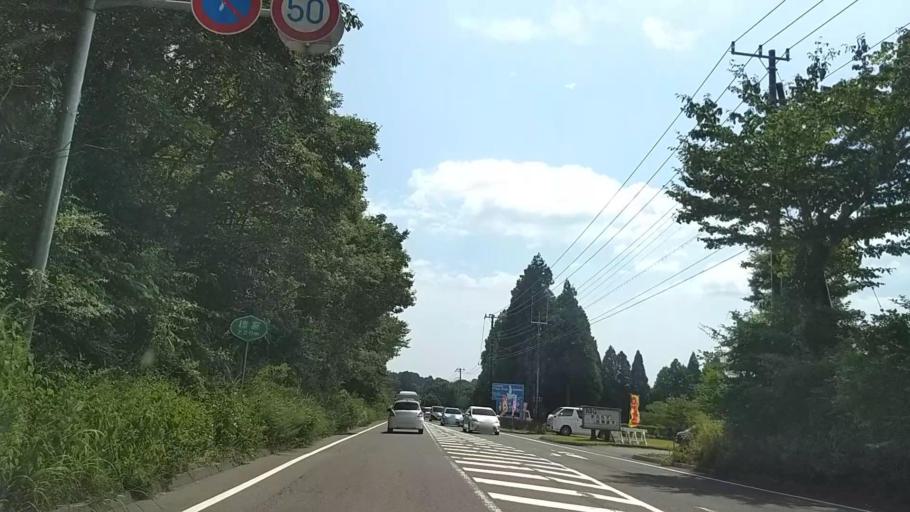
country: JP
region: Shizuoka
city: Fujinomiya
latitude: 35.3571
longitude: 138.5785
